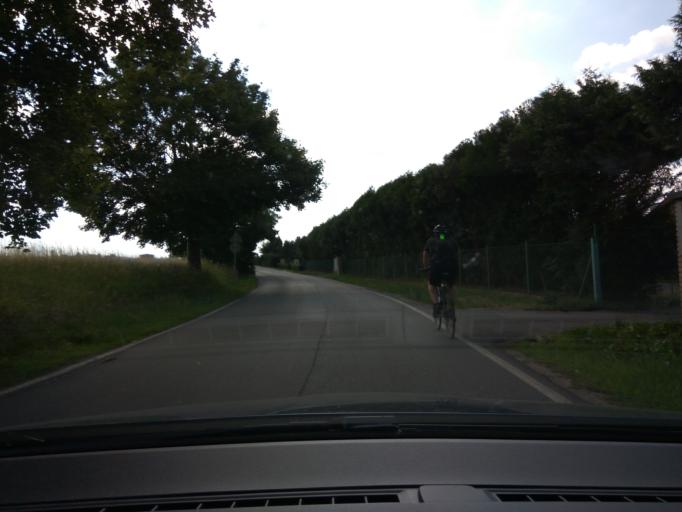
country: CZ
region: Praha
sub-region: Praha 19
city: Satalice
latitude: 50.1466
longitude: 14.5702
